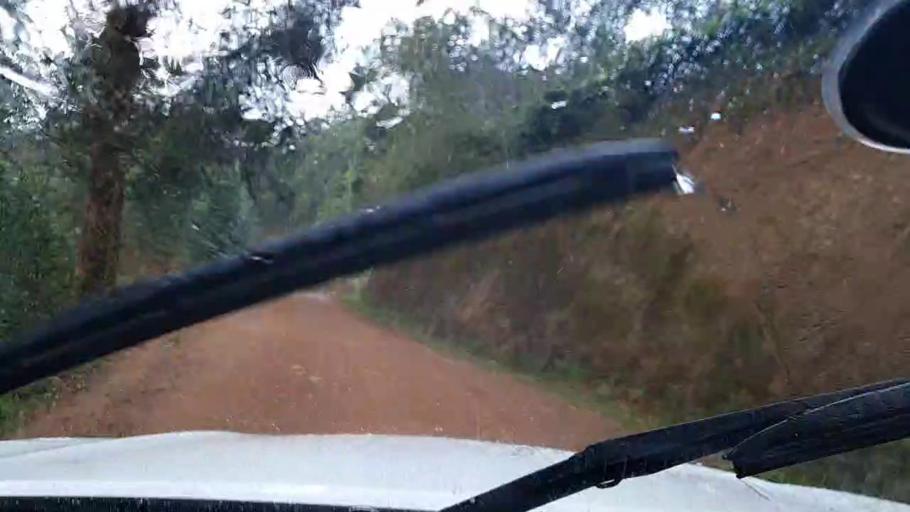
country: RW
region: Western Province
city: Kibuye
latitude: -2.1580
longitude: 29.4347
